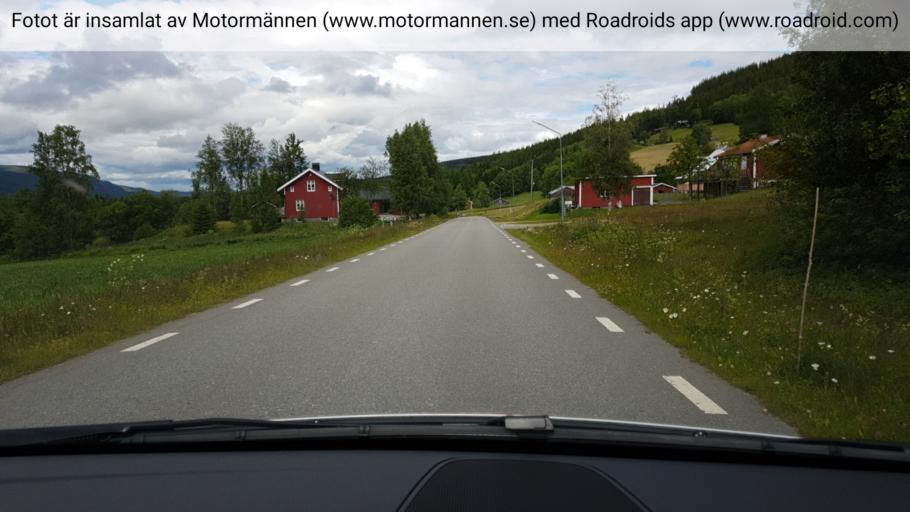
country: SE
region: Jaemtland
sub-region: Bergs Kommun
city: Hoverberg
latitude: 62.5345
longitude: 14.1848
